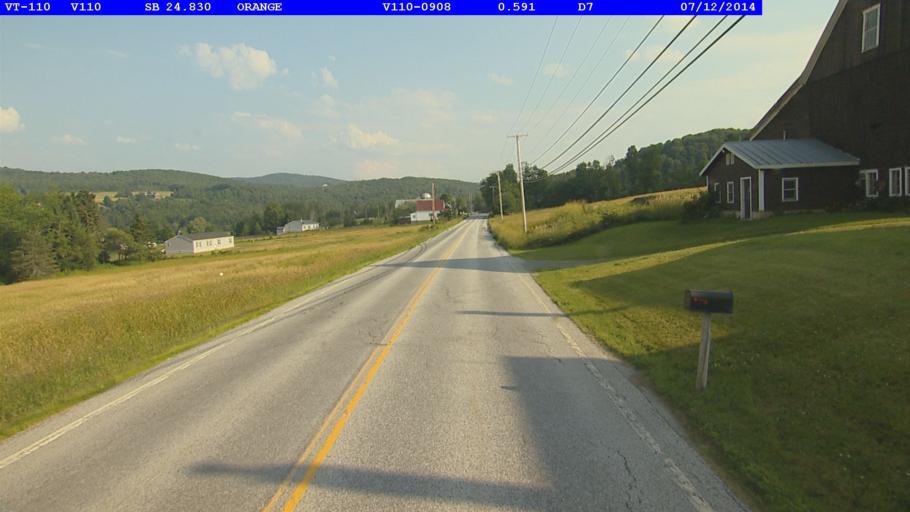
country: US
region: Vermont
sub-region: Washington County
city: South Barre
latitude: 44.1326
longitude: -72.4313
